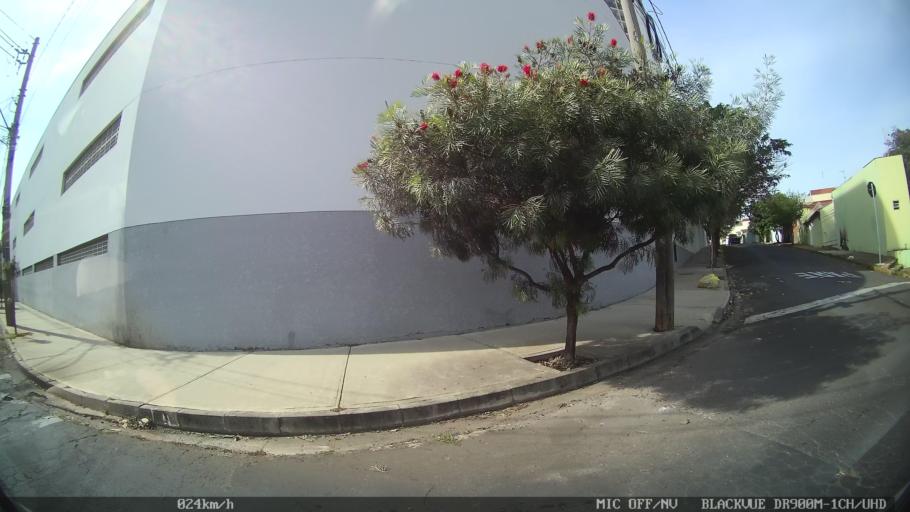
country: BR
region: Sao Paulo
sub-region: Piracicaba
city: Piracicaba
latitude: -22.7420
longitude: -47.6509
